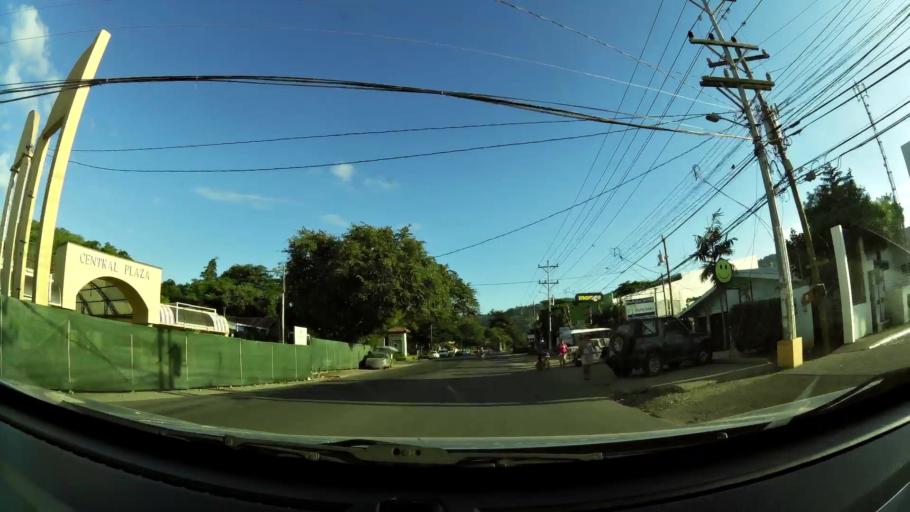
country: CR
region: Guanacaste
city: Sardinal
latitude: 10.5476
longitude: -85.6949
